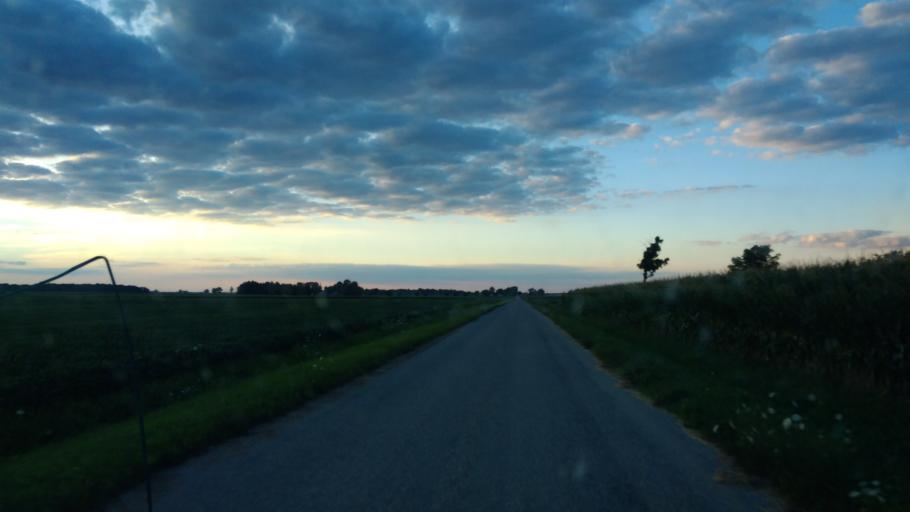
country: US
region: Indiana
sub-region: Adams County
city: Geneva
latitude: 40.6185
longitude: -85.0601
